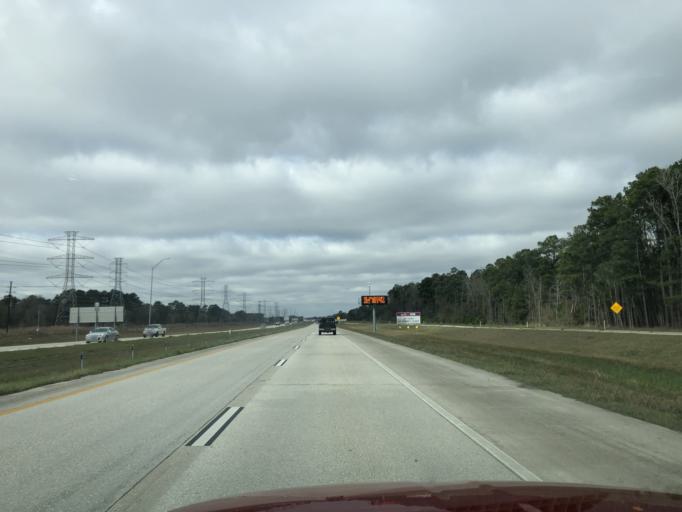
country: US
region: Texas
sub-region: Harris County
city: Spring
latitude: 30.0901
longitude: -95.4624
